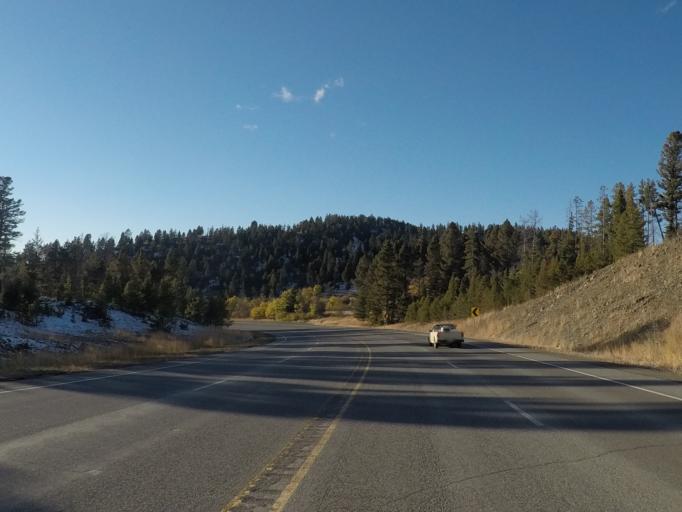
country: US
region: Montana
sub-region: Lewis and Clark County
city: Helena West Side
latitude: 46.5598
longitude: -112.3333
